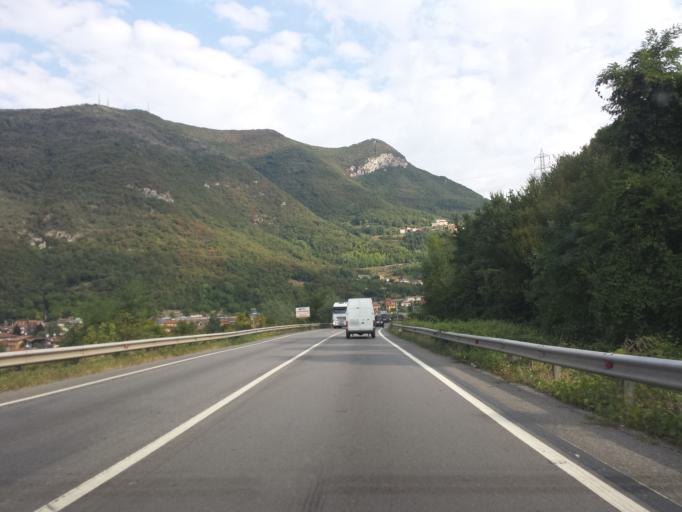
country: IT
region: Lombardy
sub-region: Provincia di Brescia
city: Villanuova sul Clisi
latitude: 45.5986
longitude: 10.4607
